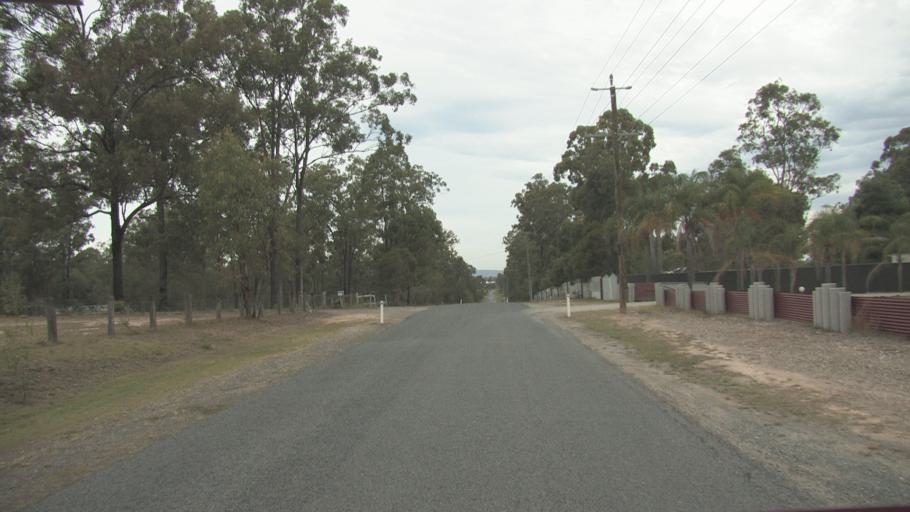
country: AU
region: Queensland
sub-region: Logan
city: Chambers Flat
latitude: -27.7968
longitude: 153.1222
